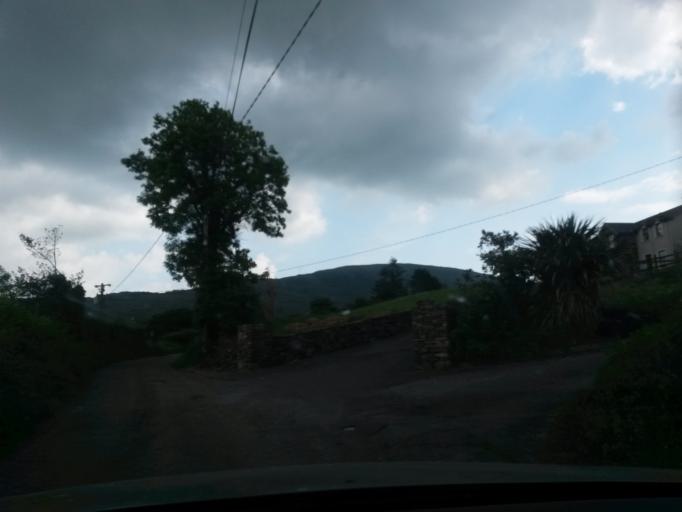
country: IE
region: Munster
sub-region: Ciarrai
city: Kenmare
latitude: 51.8594
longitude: -9.5620
